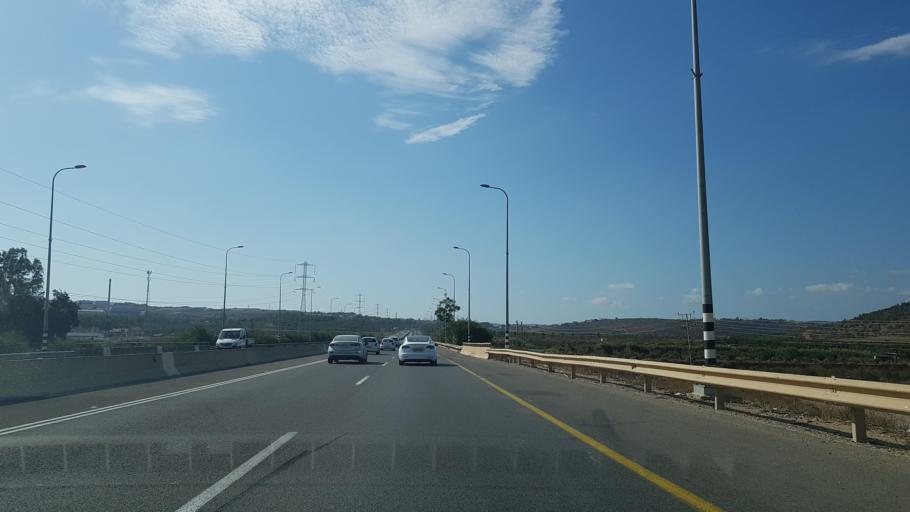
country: IL
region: Northern District
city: Kafr Kanna
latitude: 32.7629
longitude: 35.3395
